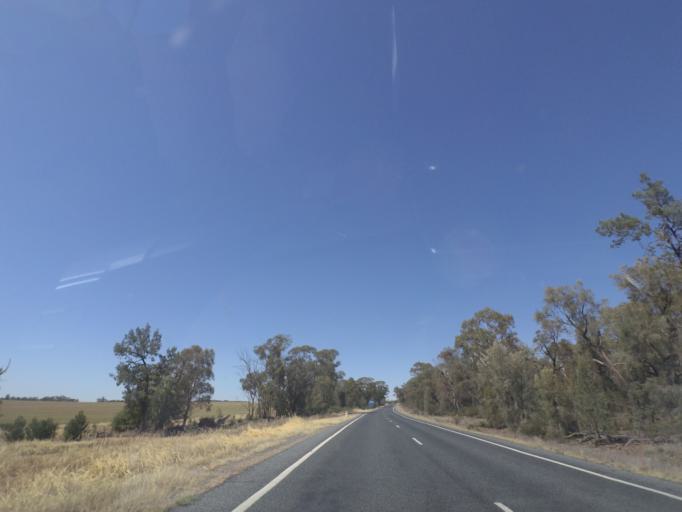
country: AU
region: New South Wales
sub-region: Narrandera
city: Narrandera
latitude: -34.4407
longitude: 146.8413
